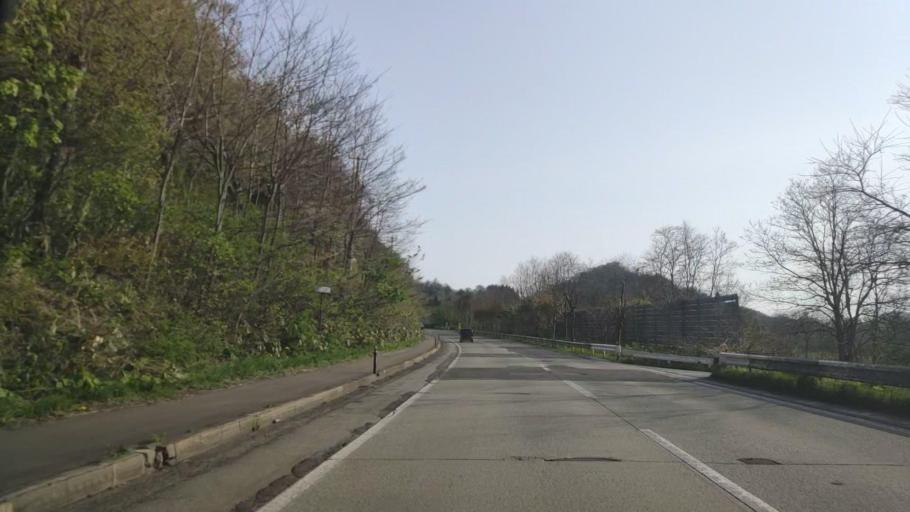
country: JP
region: Aomori
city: Aomori Shi
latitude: 40.8671
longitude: 140.8466
